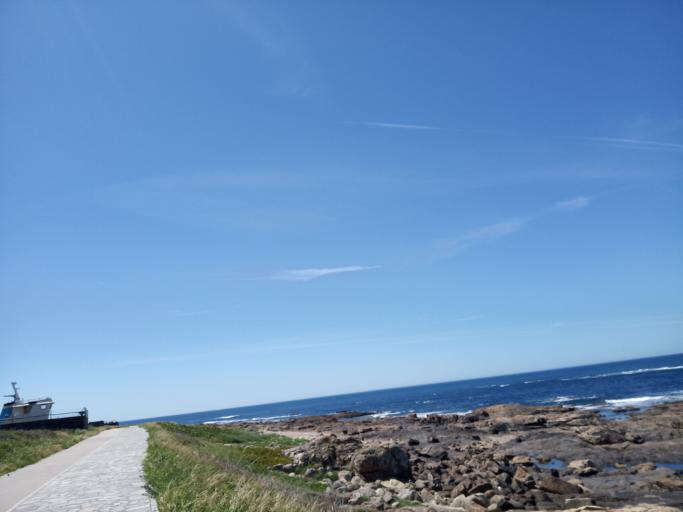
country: ES
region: Galicia
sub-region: Provincia de Pontevedra
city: A Guarda
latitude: 41.8849
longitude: -8.8812
